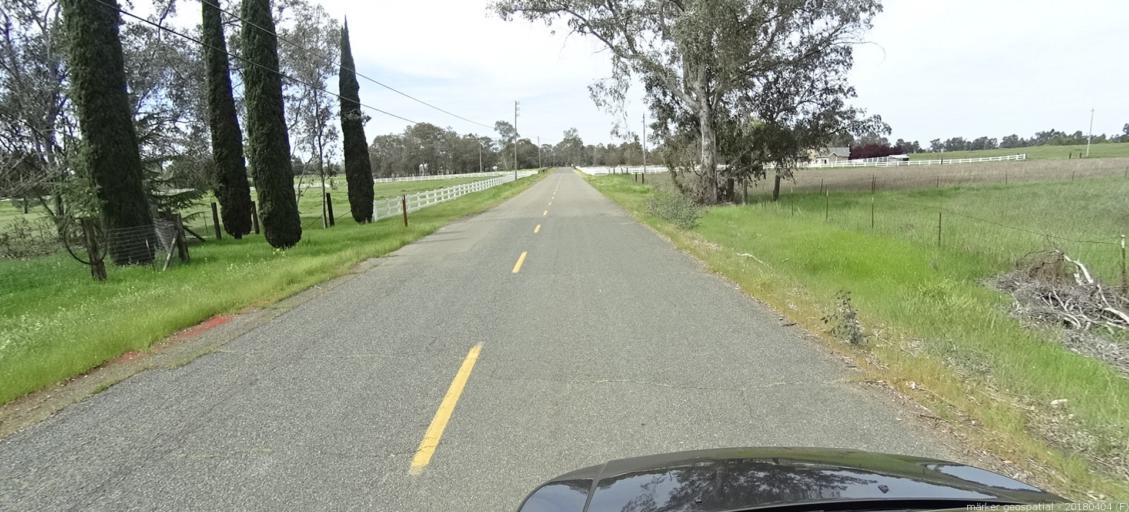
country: US
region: California
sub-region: Sacramento County
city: Clay
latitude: 38.3140
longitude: -121.1652
